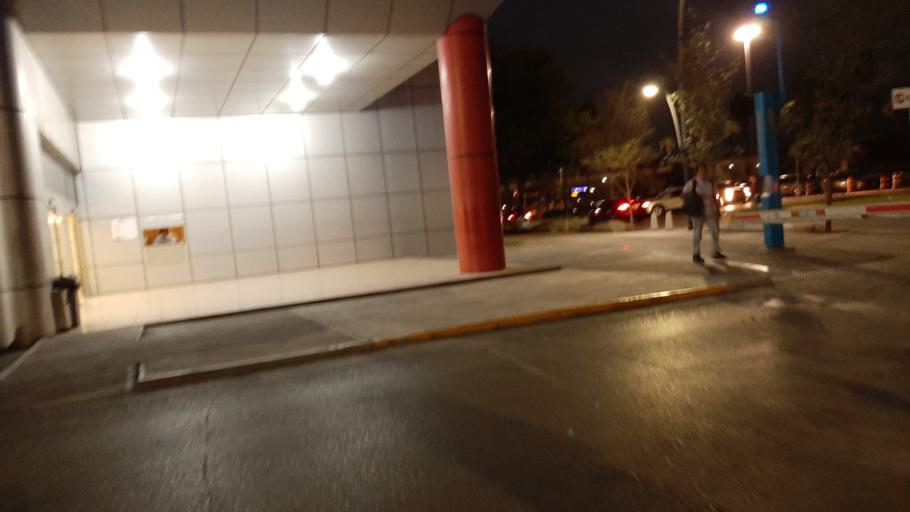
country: MX
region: Nuevo Leon
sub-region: San Nicolas de los Garza
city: San Nicolas de los Garza
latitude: 25.7237
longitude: -100.3109
